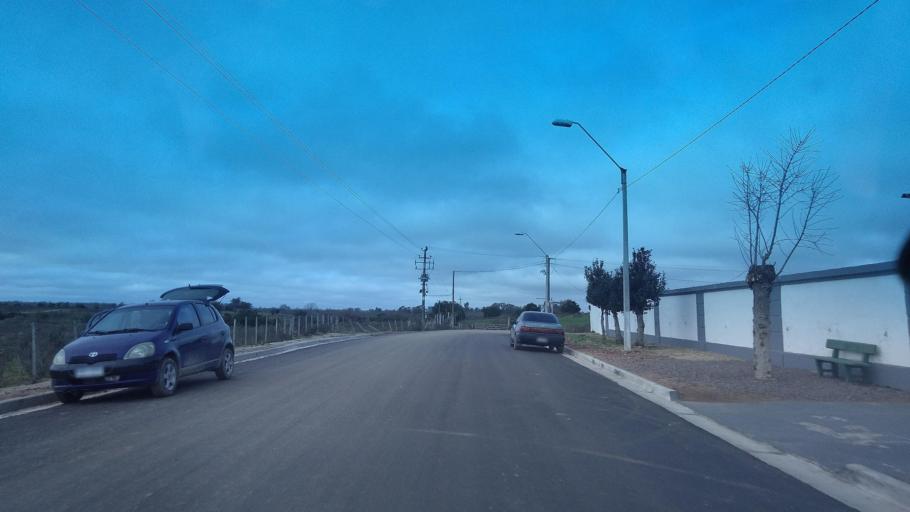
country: UY
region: Canelones
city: Tala
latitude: -34.2045
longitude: -55.7400
